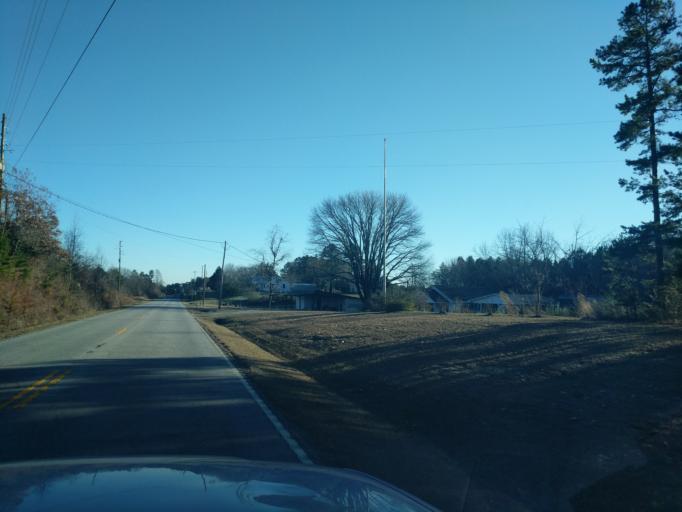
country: US
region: South Carolina
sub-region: Oconee County
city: Westminster
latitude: 34.7080
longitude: -83.1951
